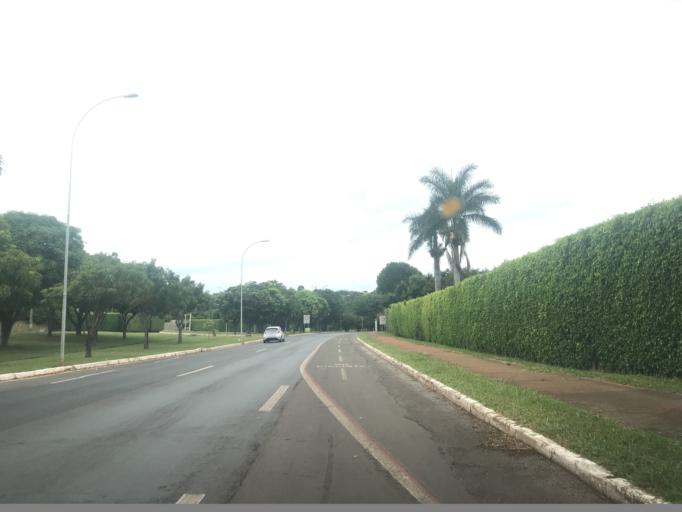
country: BR
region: Federal District
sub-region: Brasilia
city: Brasilia
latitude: -15.8387
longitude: -47.8377
